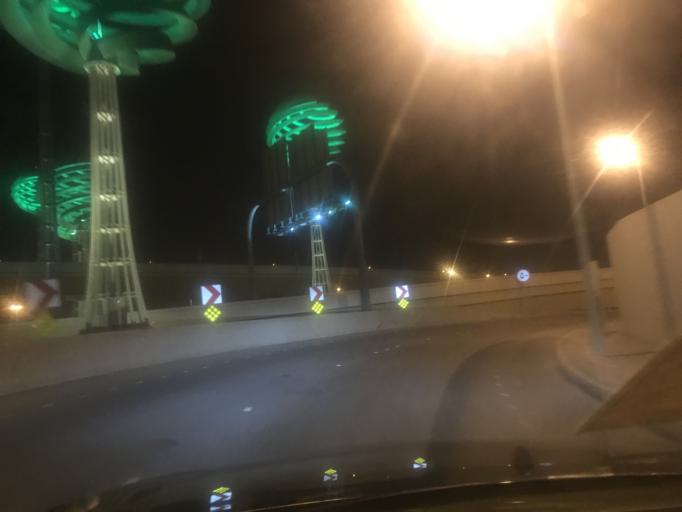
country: SA
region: Ar Riyad
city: Riyadh
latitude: 24.7040
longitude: 46.6226
